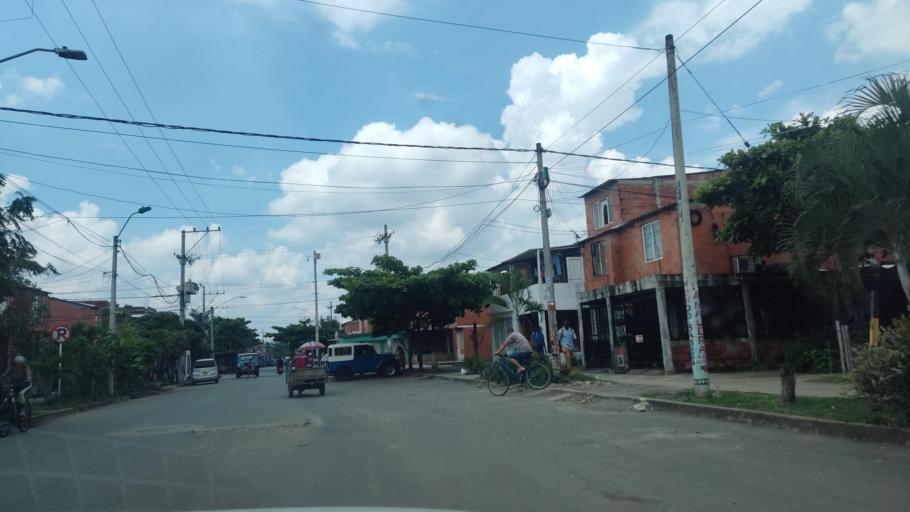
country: CO
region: Valle del Cauca
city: Cali
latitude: 3.3936
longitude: -76.5085
